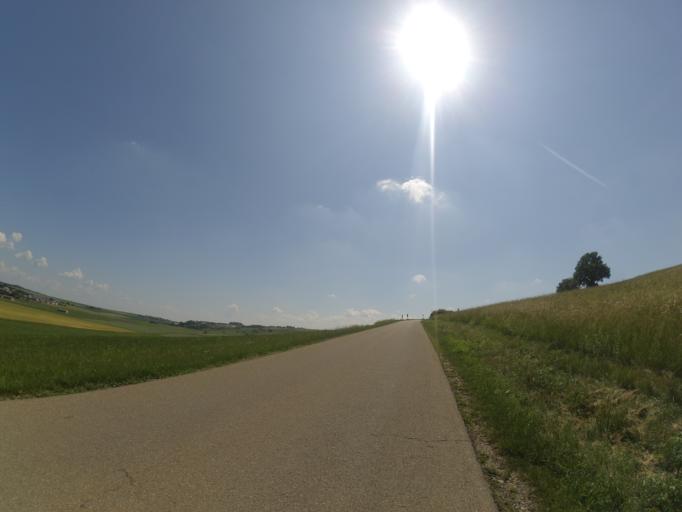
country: DE
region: Baden-Wuerttemberg
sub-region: Tuebingen Region
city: Bernstadt
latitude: 48.4767
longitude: 10.0210
